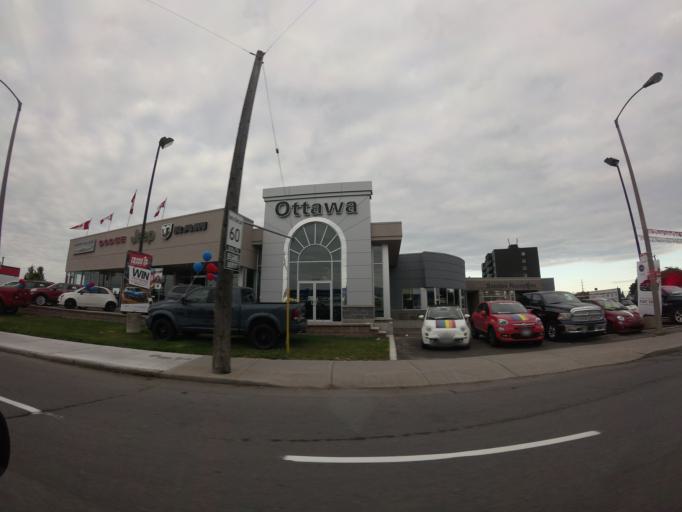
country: CA
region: Ontario
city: Ottawa
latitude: 45.4319
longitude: -75.6418
